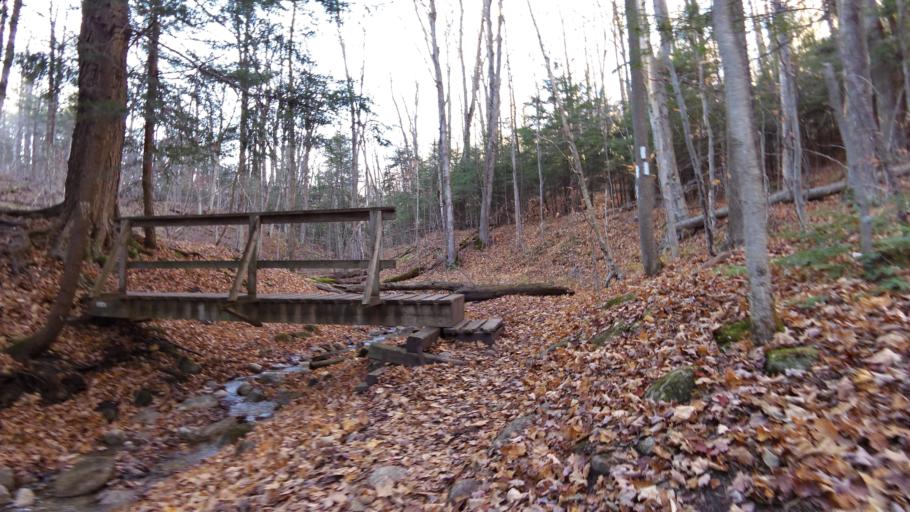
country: CA
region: Ontario
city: Orangeville
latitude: 43.9910
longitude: -80.0599
